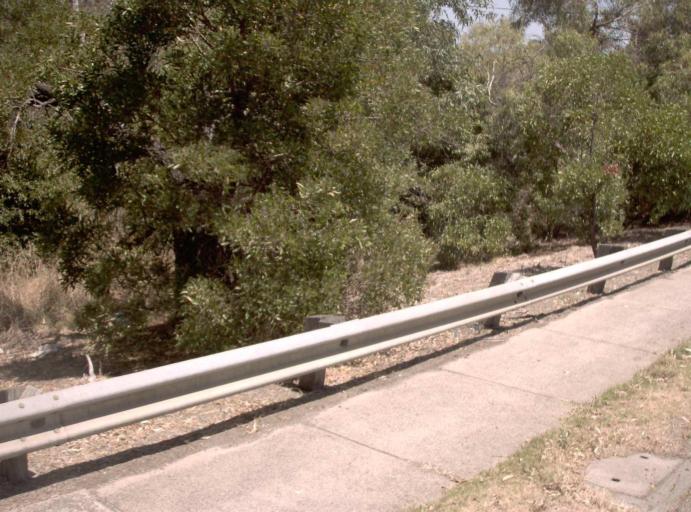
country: AU
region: Victoria
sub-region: Manningham
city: Bulleen
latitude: -37.7603
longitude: 145.0745
